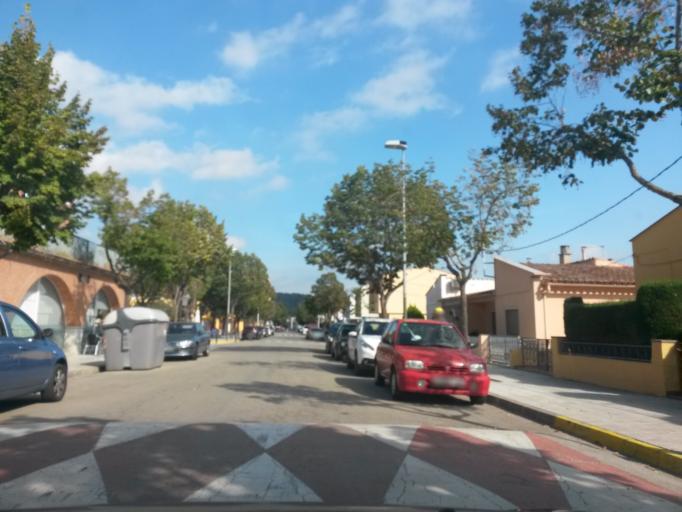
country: ES
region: Catalonia
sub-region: Provincia de Girona
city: Bescano
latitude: 41.9633
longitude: 2.7381
